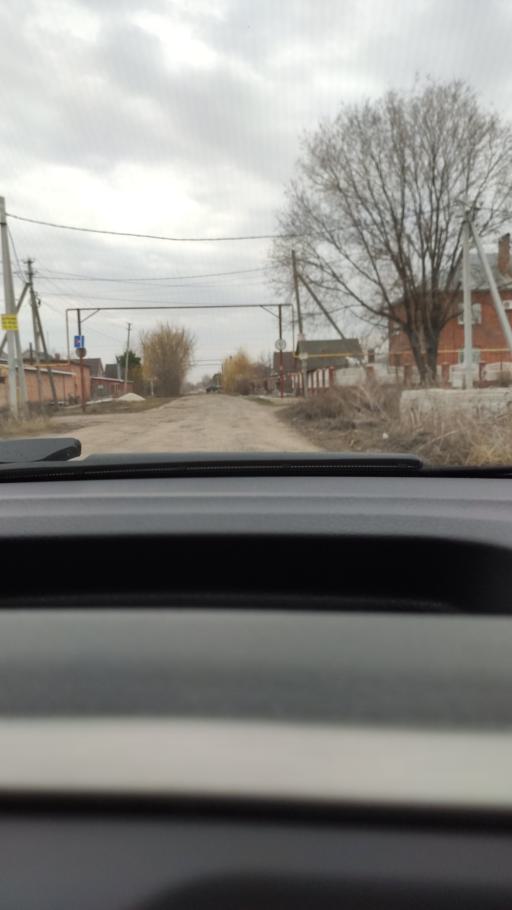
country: RU
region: Samara
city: Tol'yatti
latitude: 53.5580
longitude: 49.3874
